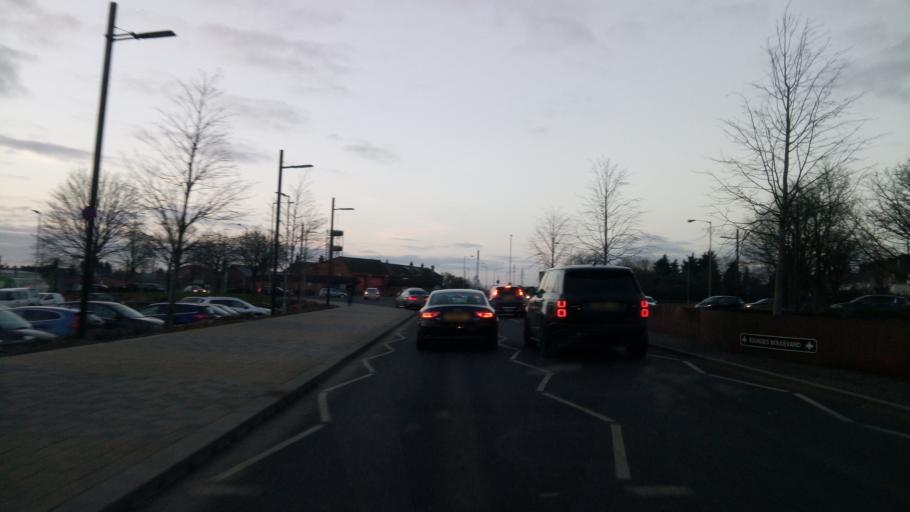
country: GB
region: England
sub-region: Peterborough
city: Peterborough
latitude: 52.5759
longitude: -0.2488
